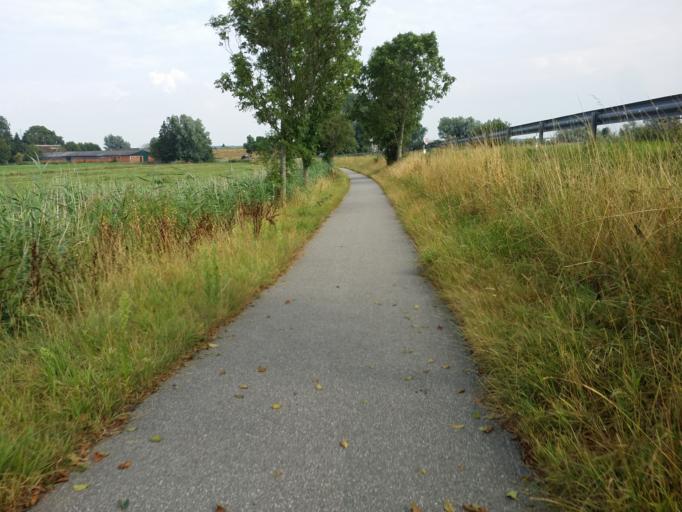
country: DE
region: Schleswig-Holstein
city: Heiligenstedten
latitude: 53.9184
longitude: 9.4885
